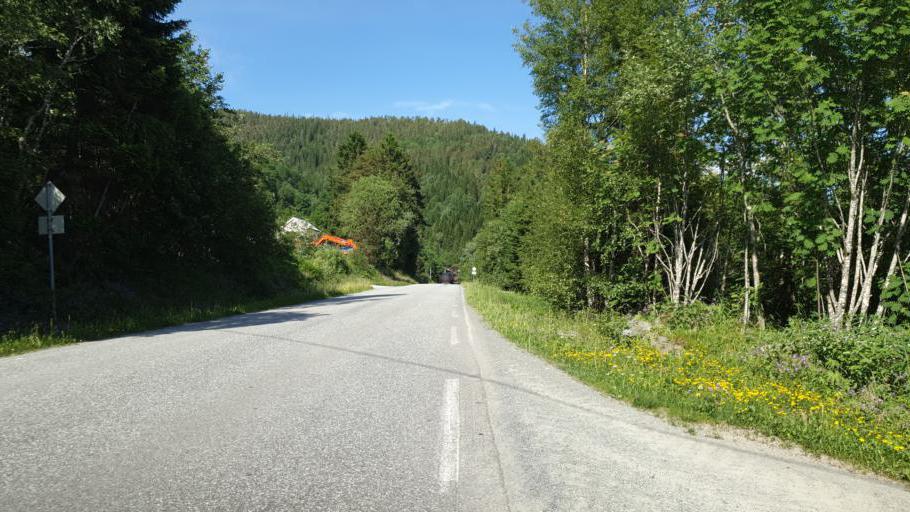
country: NO
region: Nord-Trondelag
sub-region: Leksvik
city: Leksvik
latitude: 63.6327
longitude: 10.5714
